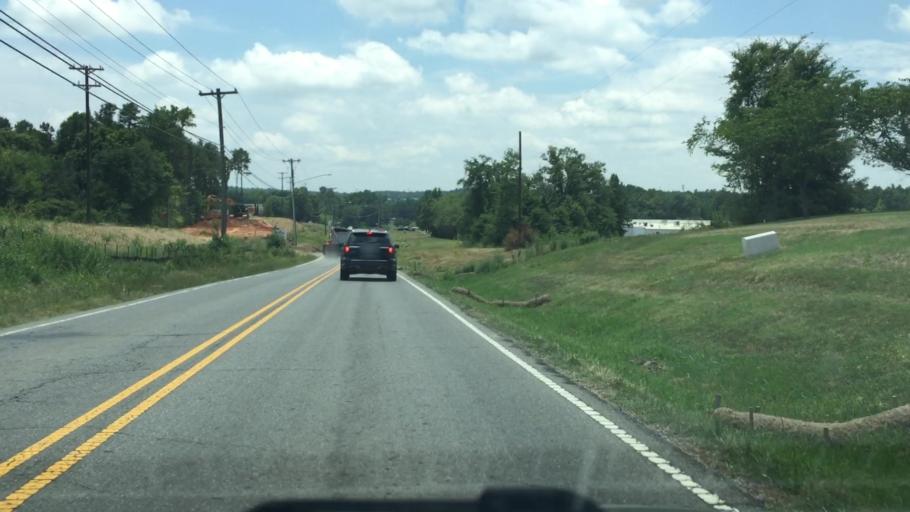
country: US
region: North Carolina
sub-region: Cabarrus County
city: Harrisburg
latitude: 35.3888
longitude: -80.7193
